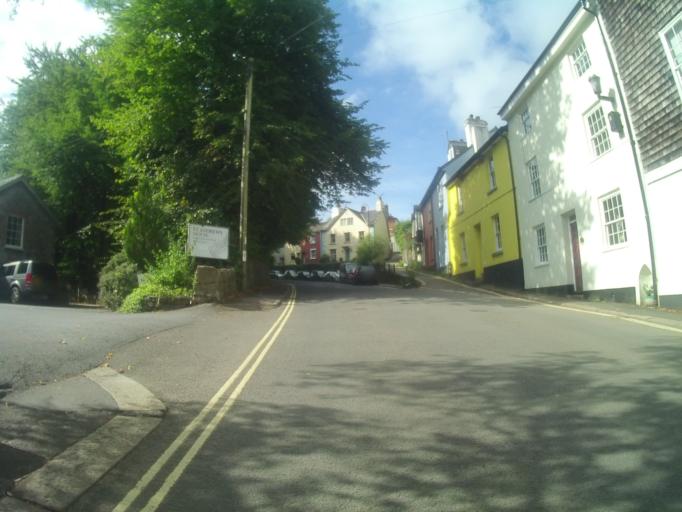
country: GB
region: England
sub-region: Devon
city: Ashburton
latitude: 50.5142
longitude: -3.7580
